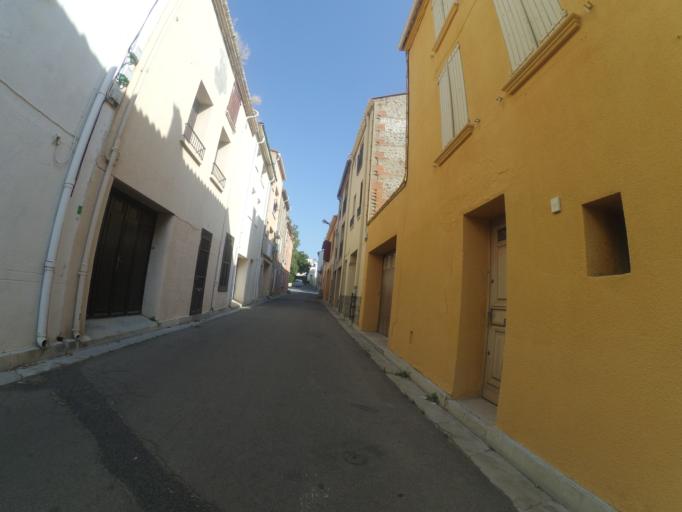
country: FR
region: Languedoc-Roussillon
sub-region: Departement des Pyrenees-Orientales
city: Saint-Esteve
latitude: 42.7075
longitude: 2.8454
